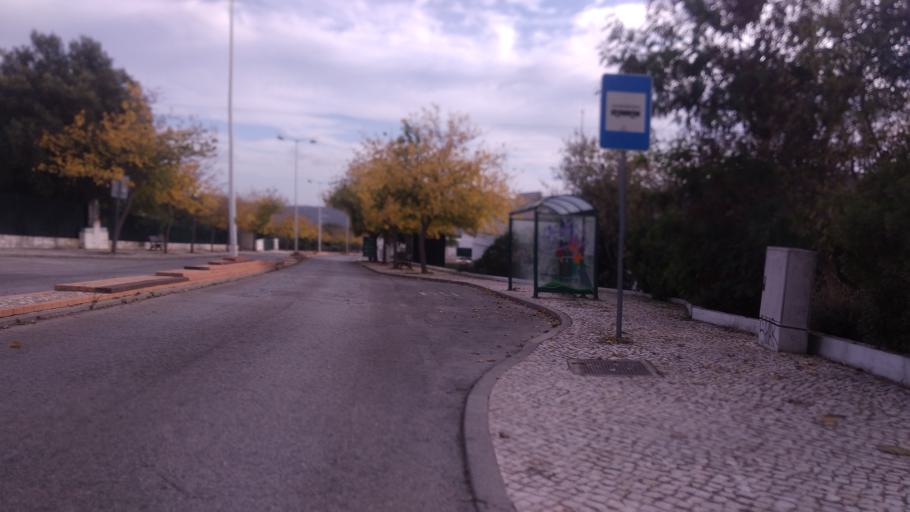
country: PT
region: Faro
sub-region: Sao Bras de Alportel
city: Sao Bras de Alportel
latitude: 37.1502
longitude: -7.8935
